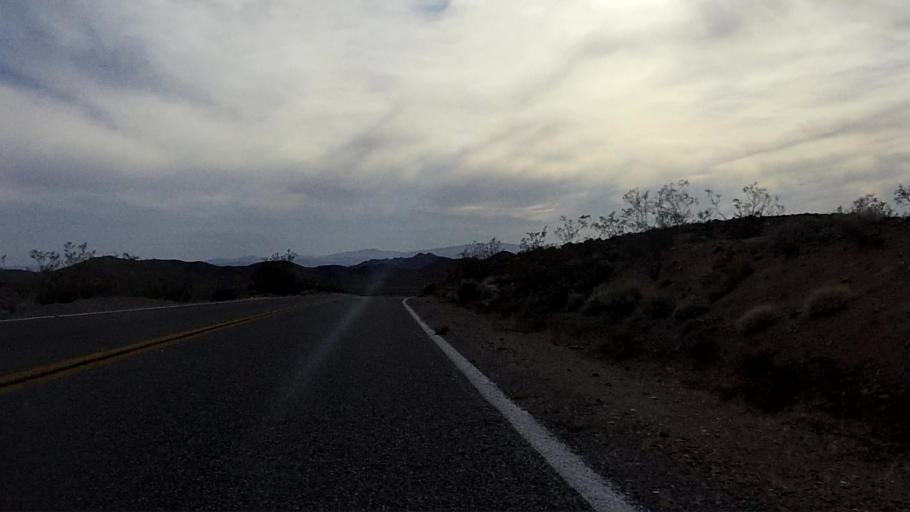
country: US
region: Nevada
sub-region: Nye County
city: Pahrump
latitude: 35.9163
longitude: -116.4394
